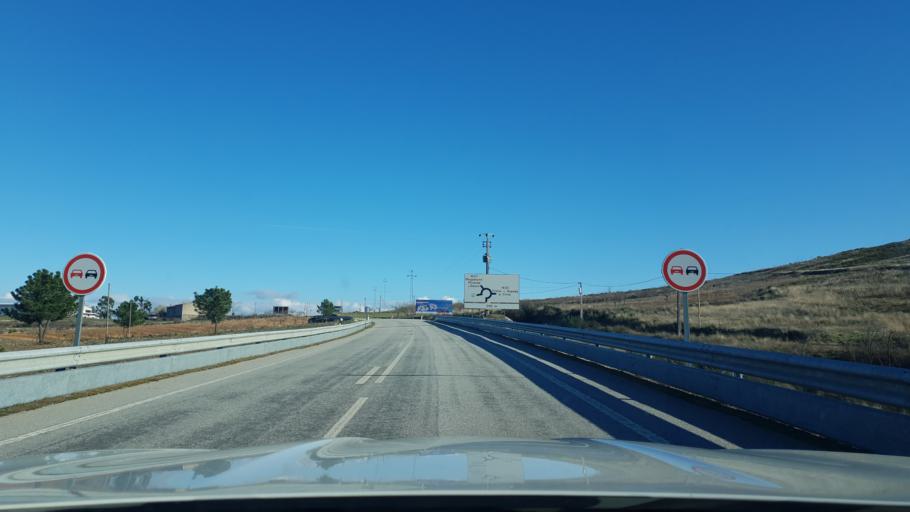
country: PT
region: Braganca
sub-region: Freixo de Espada A Cinta
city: Freixo de Espada a Cinta
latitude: 41.1780
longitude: -6.7953
